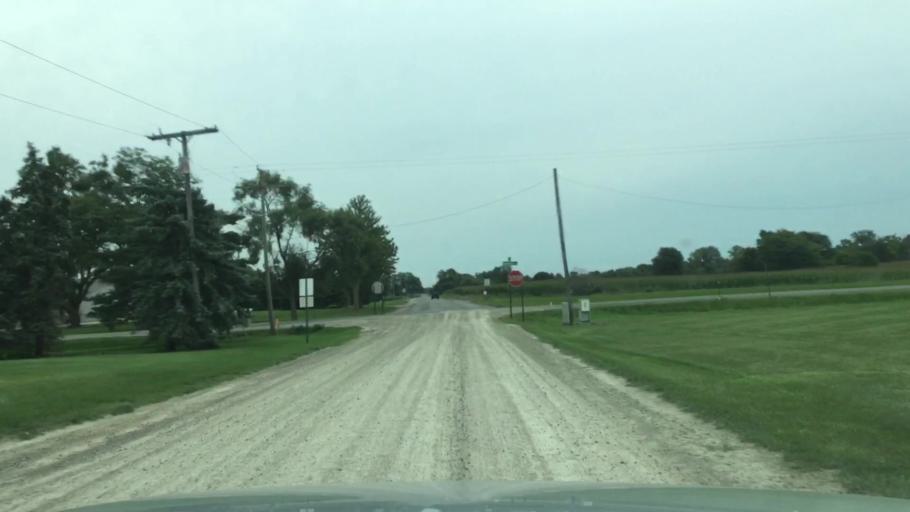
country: US
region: Michigan
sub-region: Washtenaw County
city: Milan
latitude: 42.0757
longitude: -83.7364
